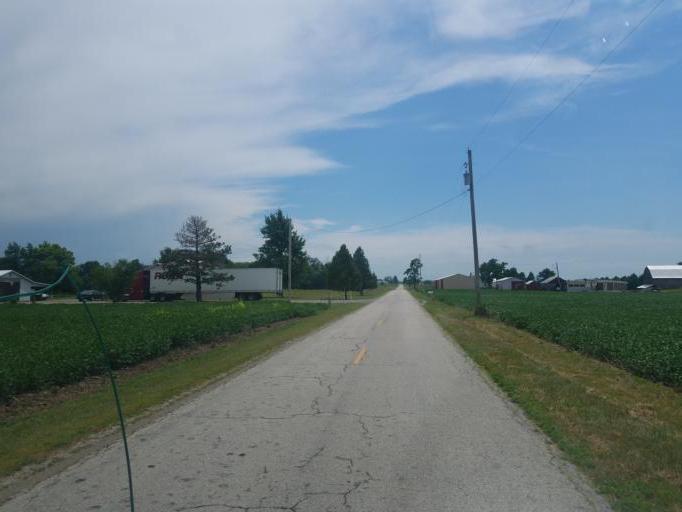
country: US
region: Ohio
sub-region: Paulding County
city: Antwerp
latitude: 41.2311
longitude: -84.7277
